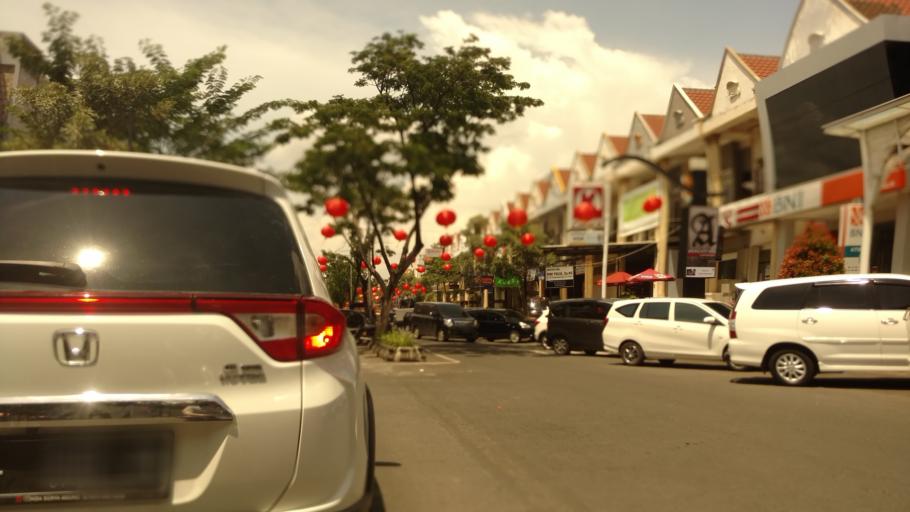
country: ID
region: East Java
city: Driyorejo
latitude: -7.2901
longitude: 112.6550
